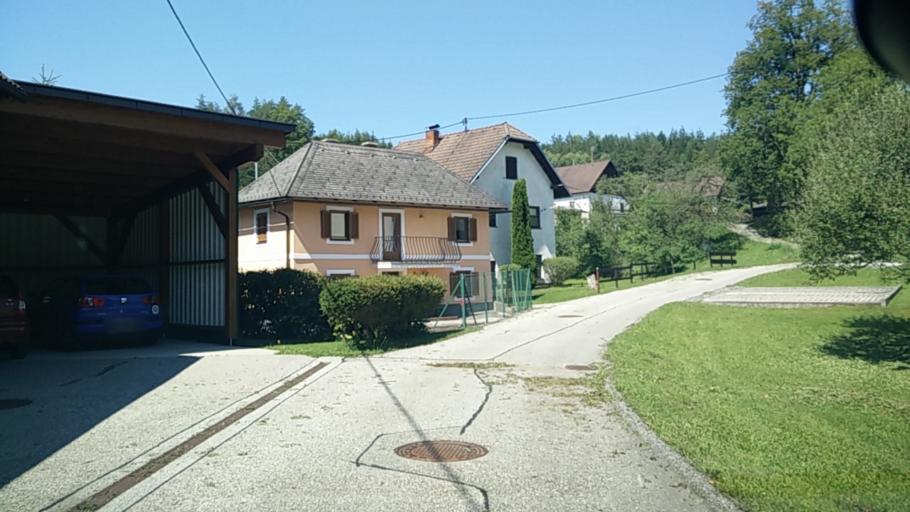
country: AT
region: Carinthia
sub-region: Politischer Bezirk Volkermarkt
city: Sittersdorf
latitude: 46.5388
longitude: 14.5931
